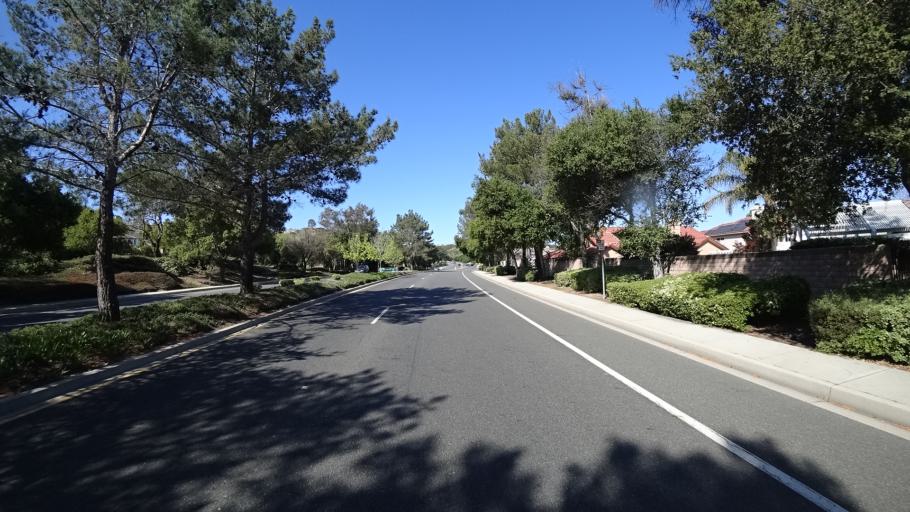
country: US
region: California
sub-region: Ventura County
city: Casa Conejo
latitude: 34.1754
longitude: -118.9236
